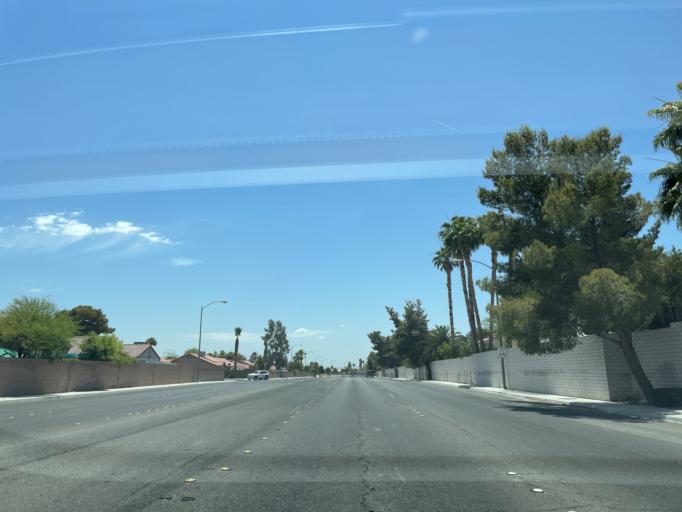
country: US
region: Nevada
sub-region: Clark County
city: North Las Vegas
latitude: 36.2681
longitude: -115.1532
